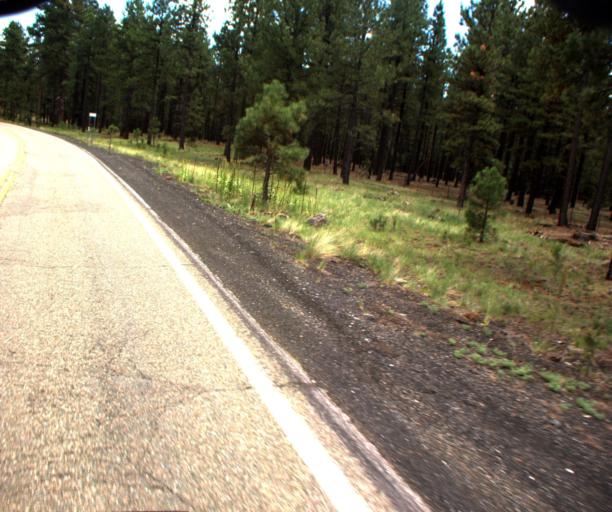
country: US
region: Arizona
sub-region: Coconino County
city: Flagstaff
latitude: 35.2883
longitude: -111.7618
